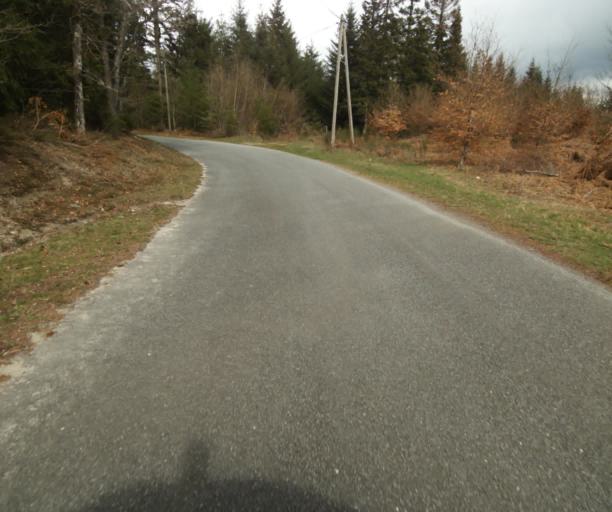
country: FR
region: Limousin
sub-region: Departement de la Correze
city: Correze
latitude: 45.2890
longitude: 1.9580
